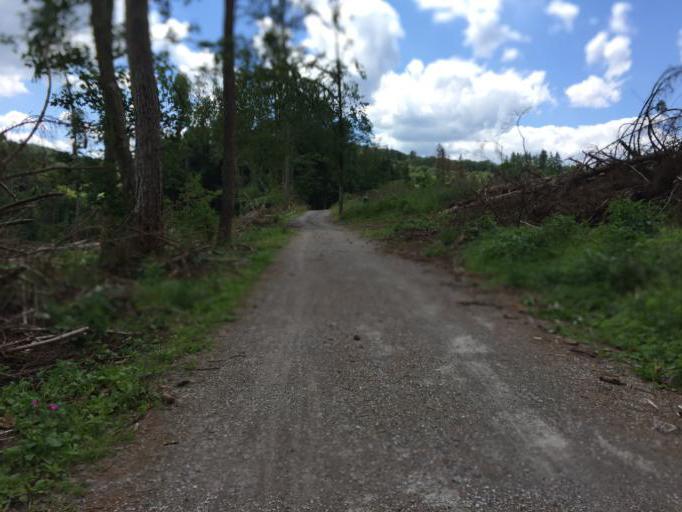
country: DE
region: Rheinland-Pfalz
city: Holler
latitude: 50.4243
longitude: 7.8573
